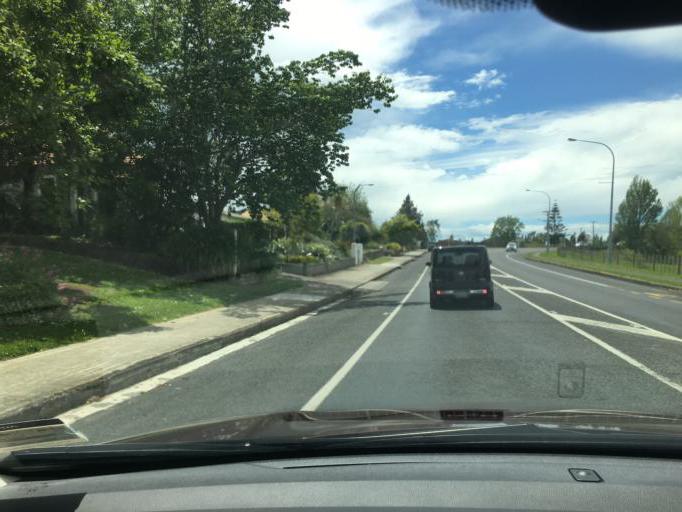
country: NZ
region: Waikato
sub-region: Hamilton City
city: Hamilton
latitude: -37.9177
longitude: 175.3067
